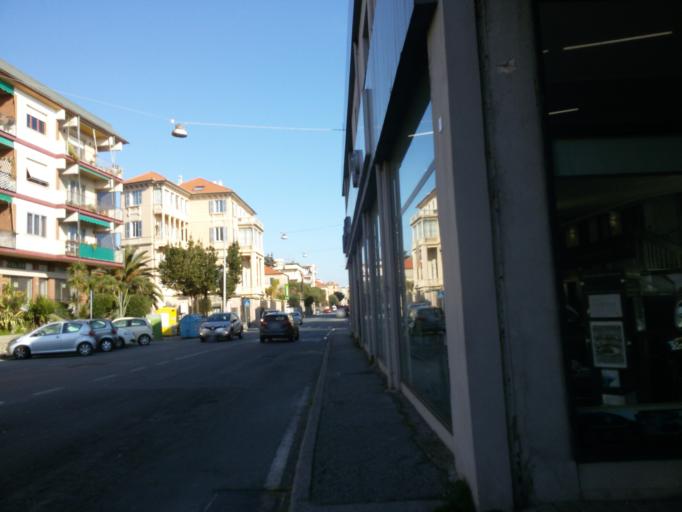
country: IT
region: Liguria
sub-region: Provincia di Savona
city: Savona
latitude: 44.2945
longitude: 8.4588
